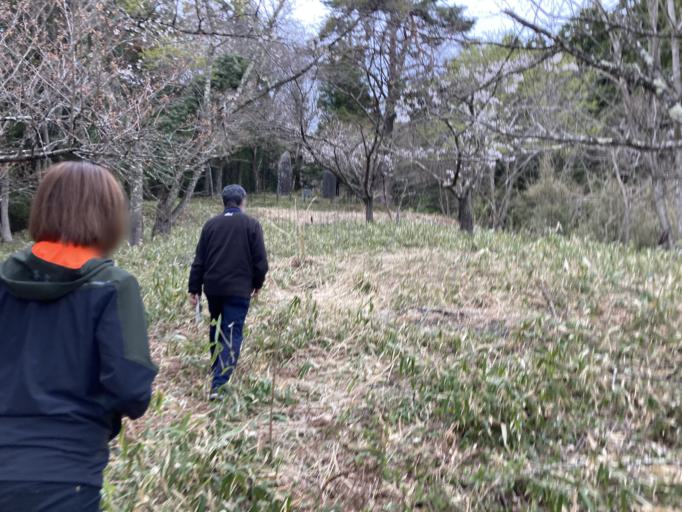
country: JP
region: Iwate
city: Ichinoseki
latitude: 38.9686
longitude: 141.1908
